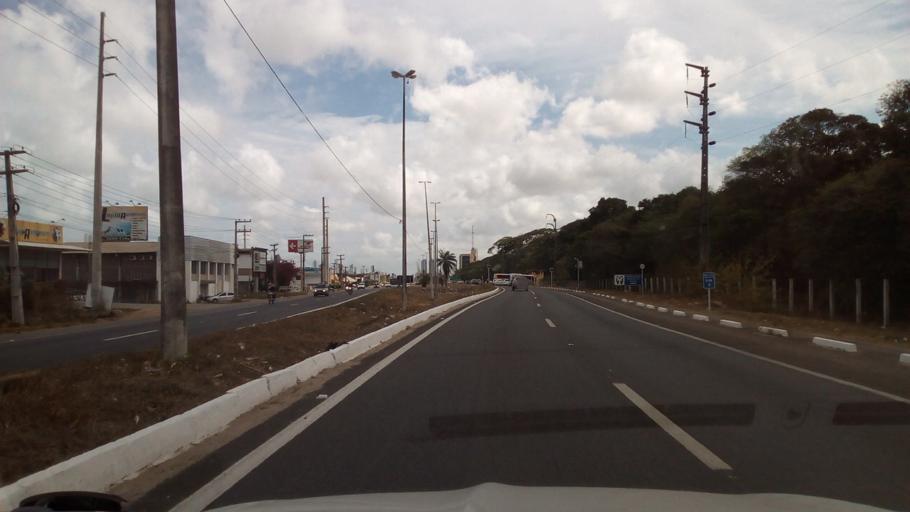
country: BR
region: Paraiba
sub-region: Joao Pessoa
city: Joao Pessoa
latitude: -7.0624
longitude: -34.8504
